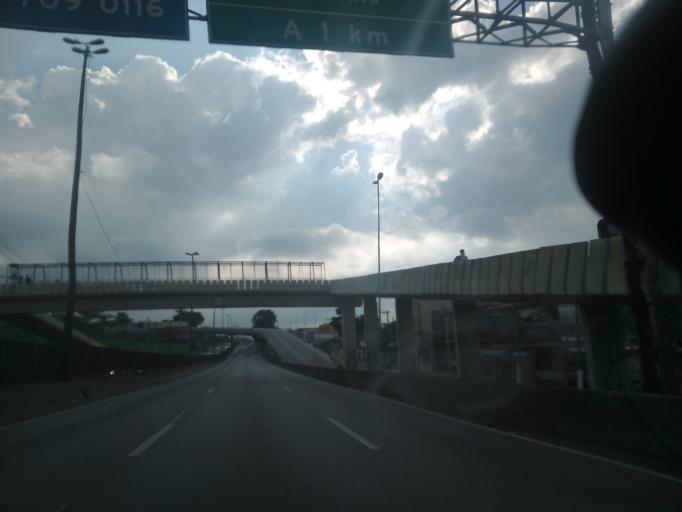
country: BR
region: Sao Paulo
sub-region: Taboao Da Serra
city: Taboao da Serra
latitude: -23.6114
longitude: -46.7760
